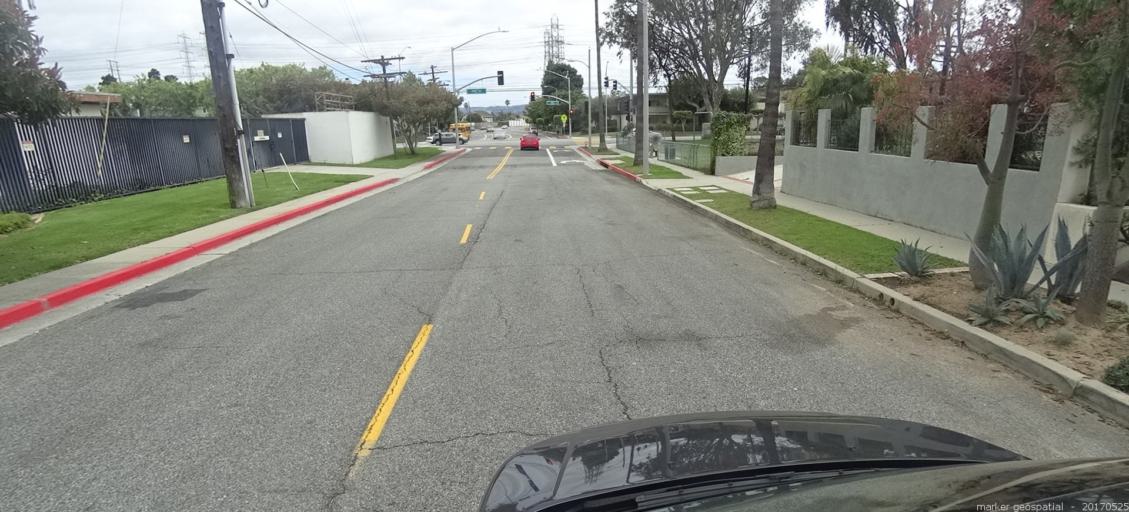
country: US
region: California
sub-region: Los Angeles County
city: Redondo Beach
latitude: 33.8590
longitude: -118.3749
